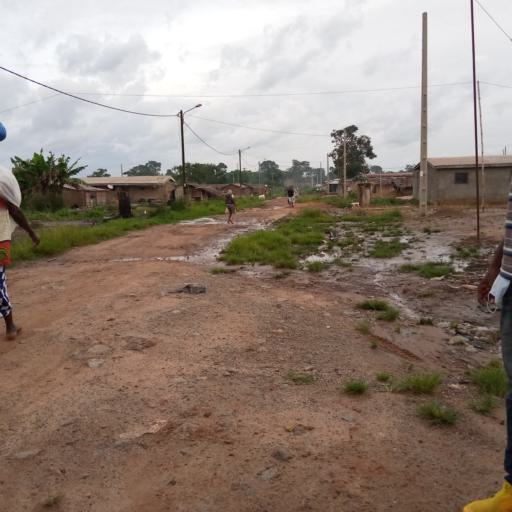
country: CI
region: Sud-Bandama
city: Divo
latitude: 5.5233
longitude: -5.2358
